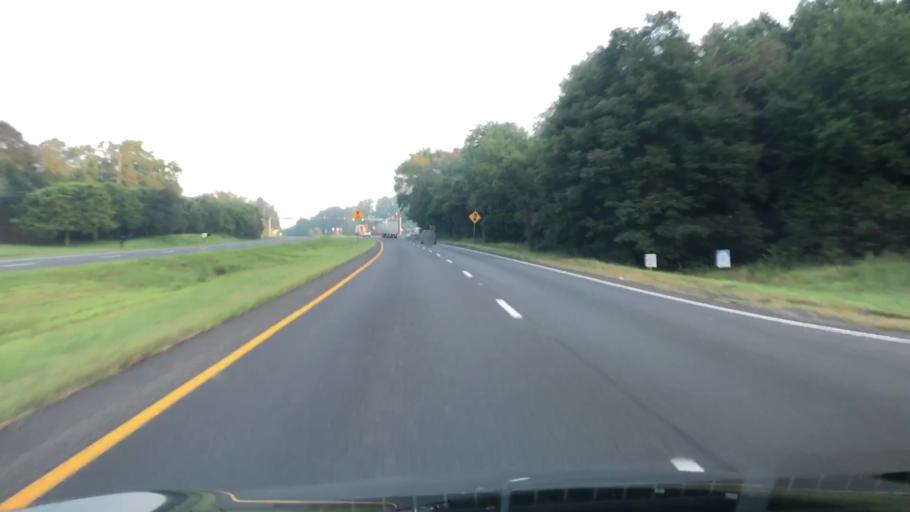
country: US
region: Virginia
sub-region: Fauquier County
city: Bealeton
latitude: 38.4984
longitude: -77.6900
